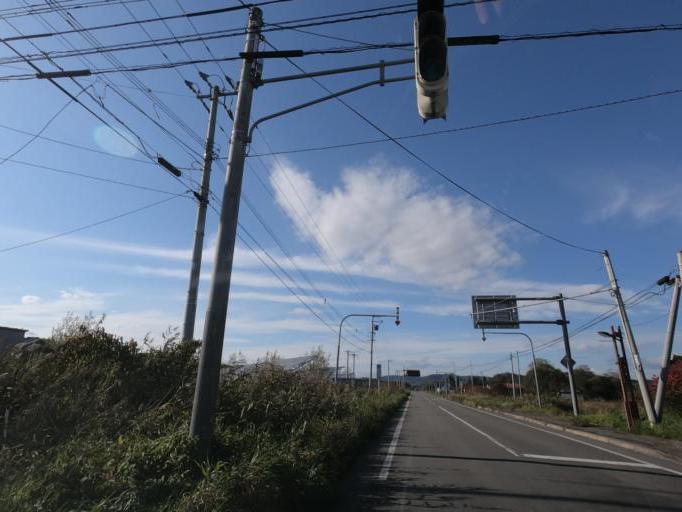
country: JP
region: Hokkaido
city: Obihiro
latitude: 42.5990
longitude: 143.4516
